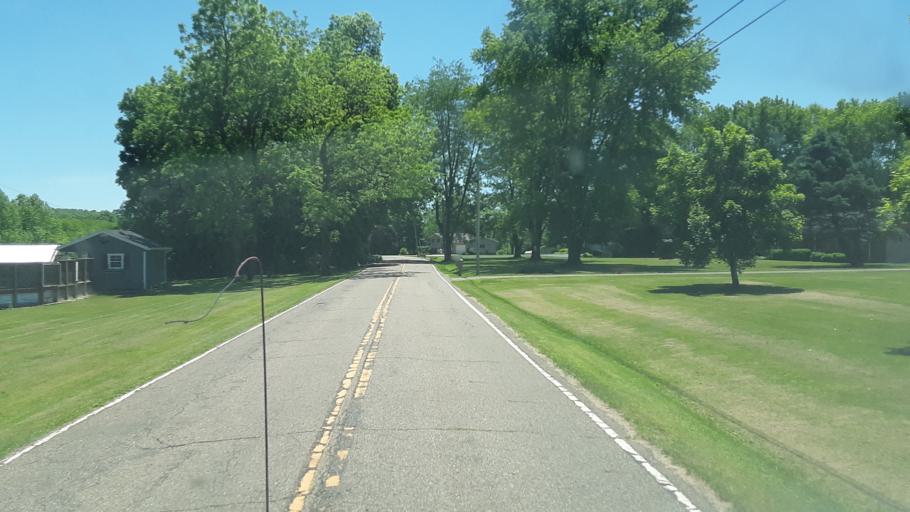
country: US
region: Ohio
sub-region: Coshocton County
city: Coshocton
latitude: 40.3019
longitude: -82.0105
